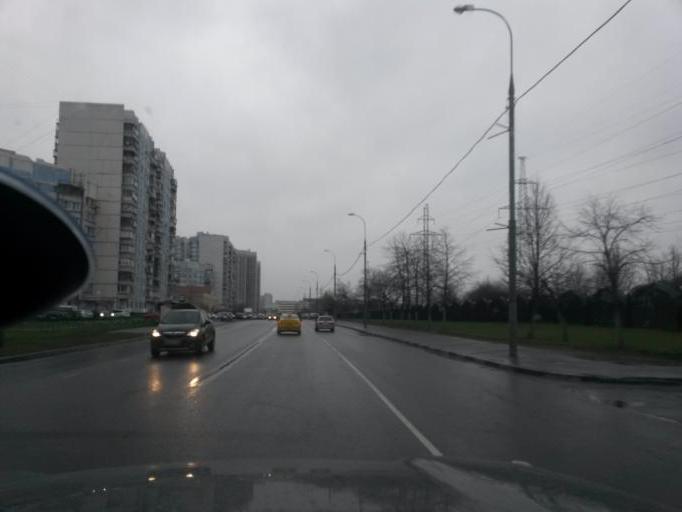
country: RU
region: Moscow
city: Brateyevo
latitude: 55.6456
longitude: 37.7570
